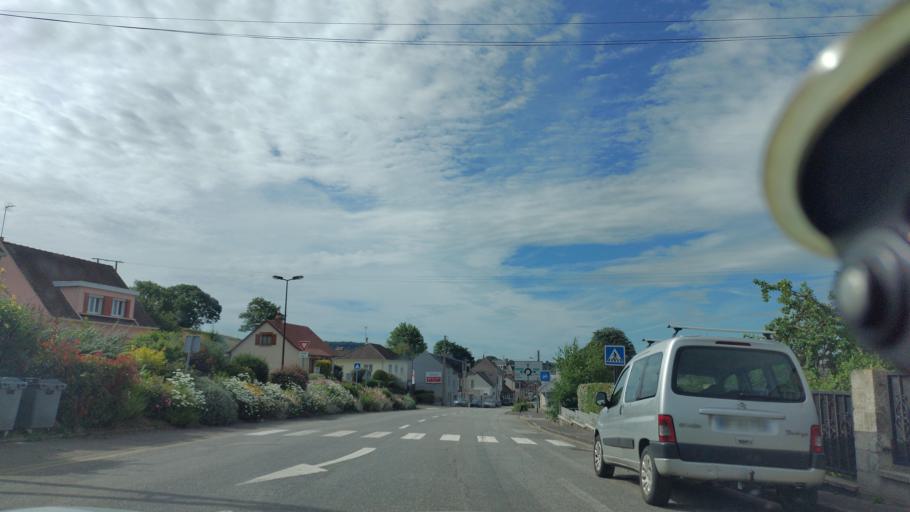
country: FR
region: Haute-Normandie
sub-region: Departement de la Seine-Maritime
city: Eu
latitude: 50.0589
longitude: 1.4244
